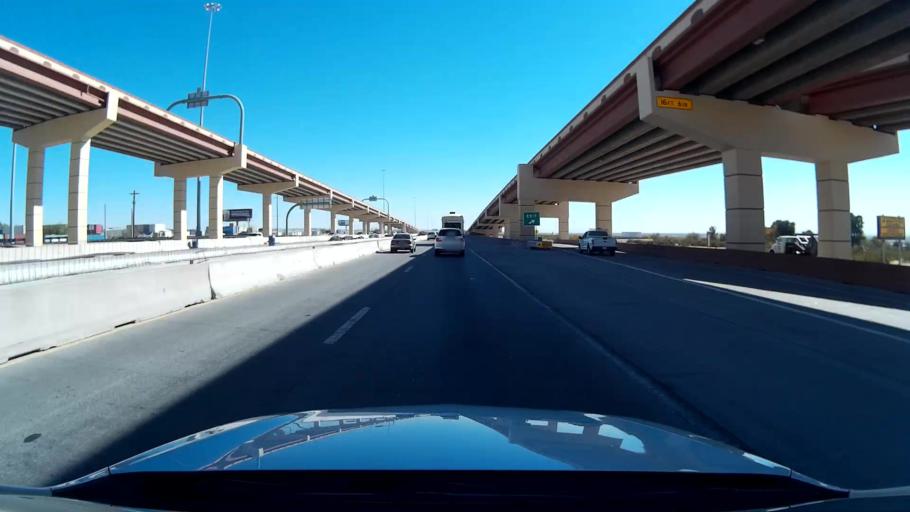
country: US
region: Texas
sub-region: El Paso County
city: Socorro
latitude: 31.6993
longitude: -106.2822
